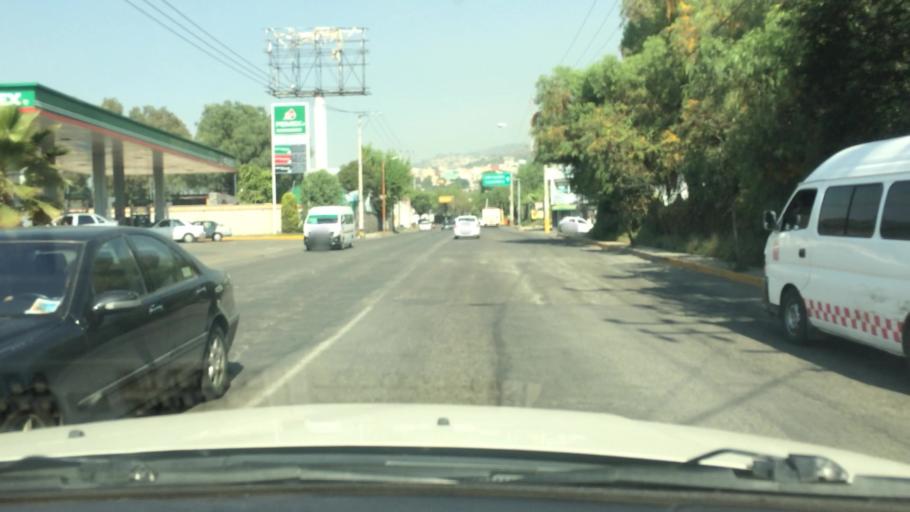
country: MX
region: Mexico
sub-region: Tlalnepantla de Baz
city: Puerto Escondido (Tepeolulco Puerto Escondido)
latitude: 19.5245
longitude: -99.1030
